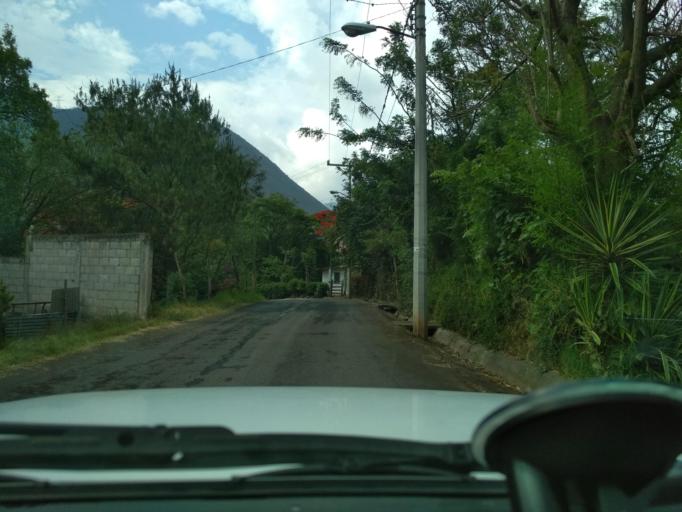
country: MX
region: Veracruz
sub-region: Nogales
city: Taza de Agua Ojo Zarco
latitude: 18.7848
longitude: -97.2001
